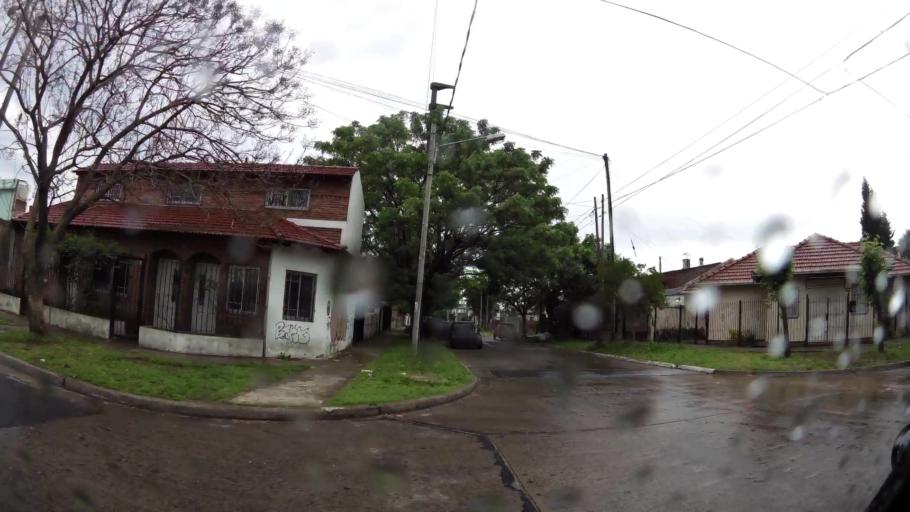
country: AR
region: Buenos Aires
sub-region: Partido de Quilmes
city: Quilmes
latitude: -34.7653
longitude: -58.2266
